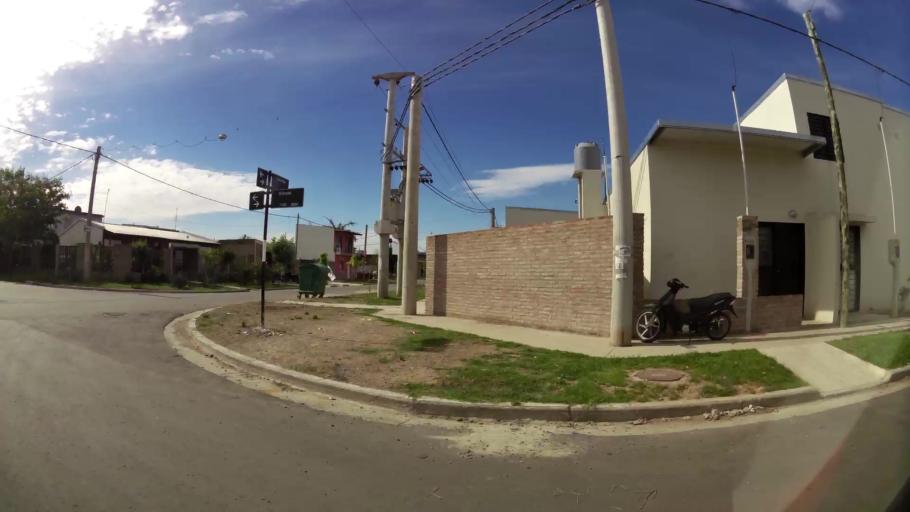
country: AR
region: Santa Fe
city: Granadero Baigorria
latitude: -32.9126
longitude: -60.7176
